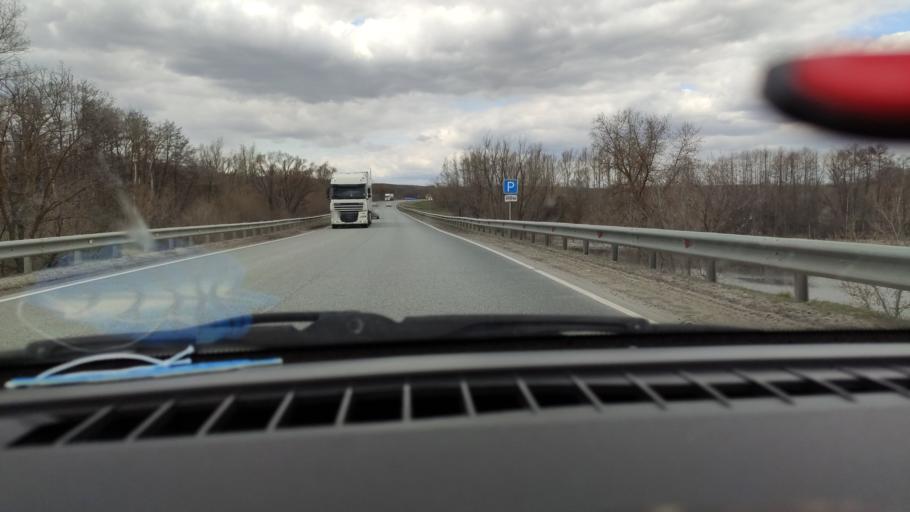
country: RU
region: Saratov
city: Tersa
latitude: 52.1024
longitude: 47.4737
